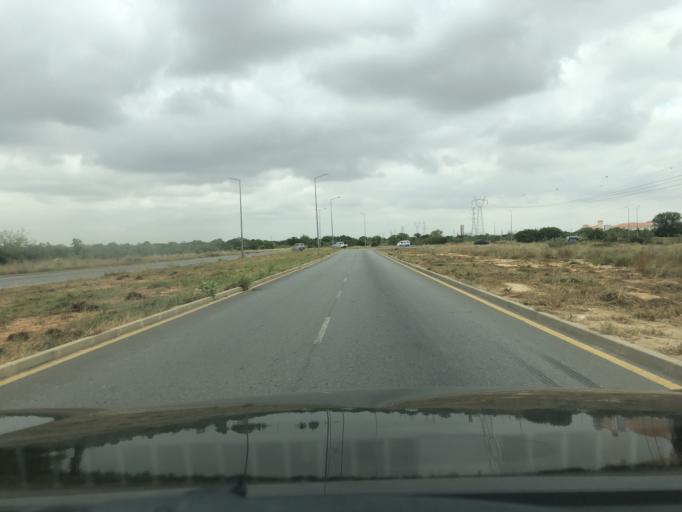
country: AO
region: Luanda
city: Luanda
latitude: -8.9757
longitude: 13.2787
